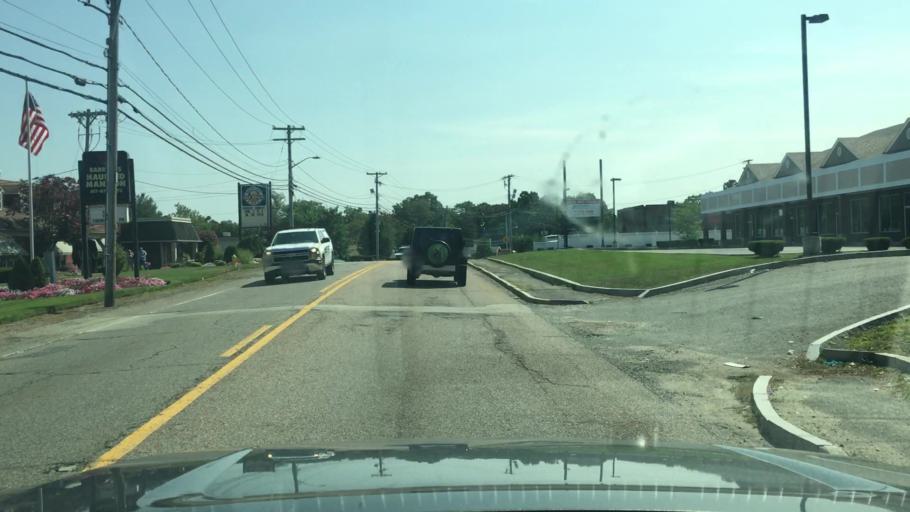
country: US
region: Massachusetts
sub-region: Plymouth County
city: Abington
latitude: 42.1386
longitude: -70.9508
